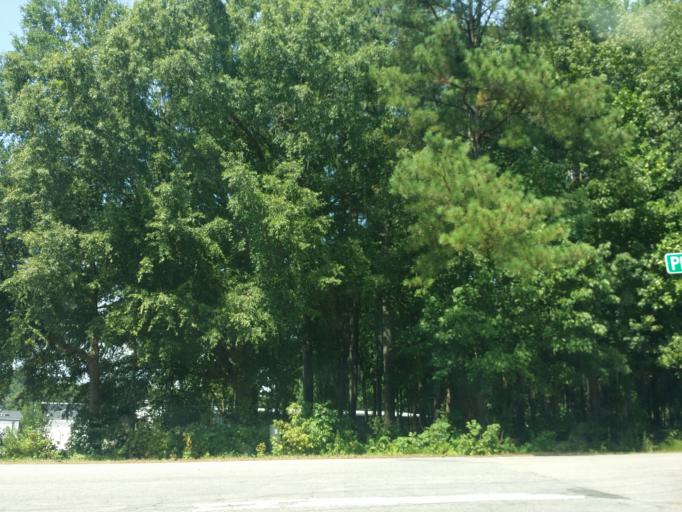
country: US
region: North Carolina
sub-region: Wake County
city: West Raleigh
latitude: 35.8645
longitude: -78.7123
